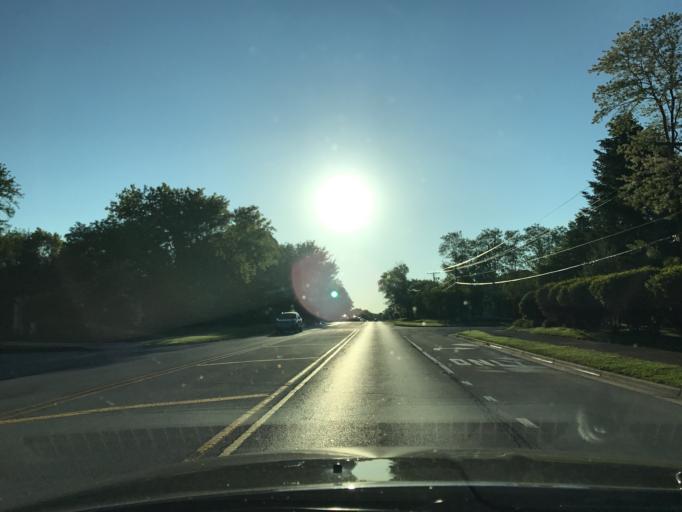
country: US
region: Illinois
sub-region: DuPage County
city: Naperville
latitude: 41.7541
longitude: -88.1117
